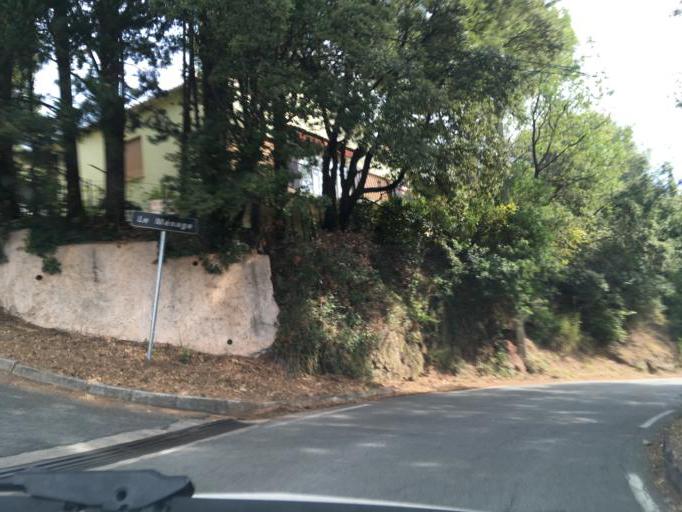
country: FR
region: Provence-Alpes-Cote d'Azur
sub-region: Departement du Var
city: Taradeau
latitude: 43.4556
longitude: 6.4274
